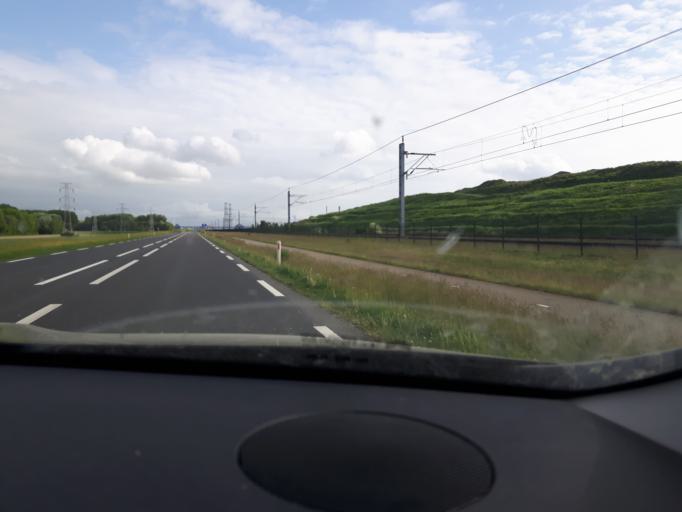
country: NL
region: Zeeland
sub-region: Gemeente Borsele
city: Borssele
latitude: 51.4696
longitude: 3.7254
